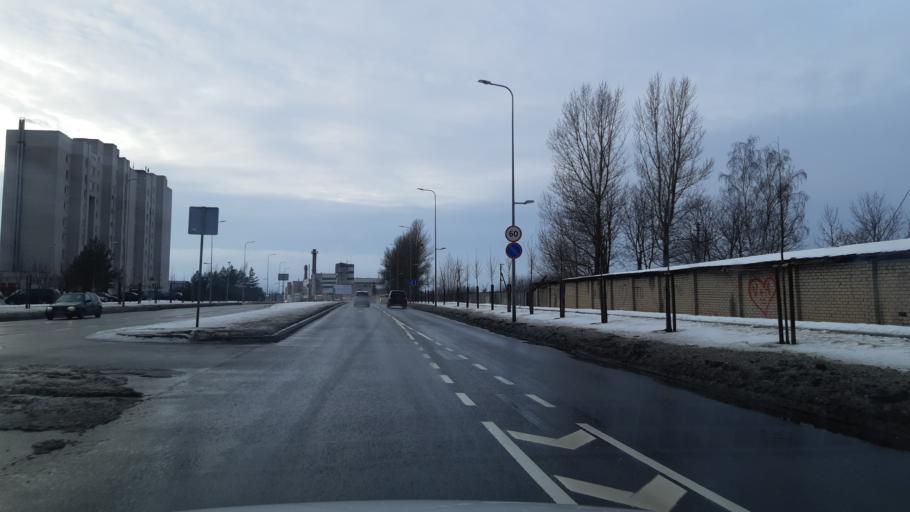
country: LT
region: Kauno apskritis
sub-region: Kaunas
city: Aleksotas
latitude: 54.8753
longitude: 23.9083
